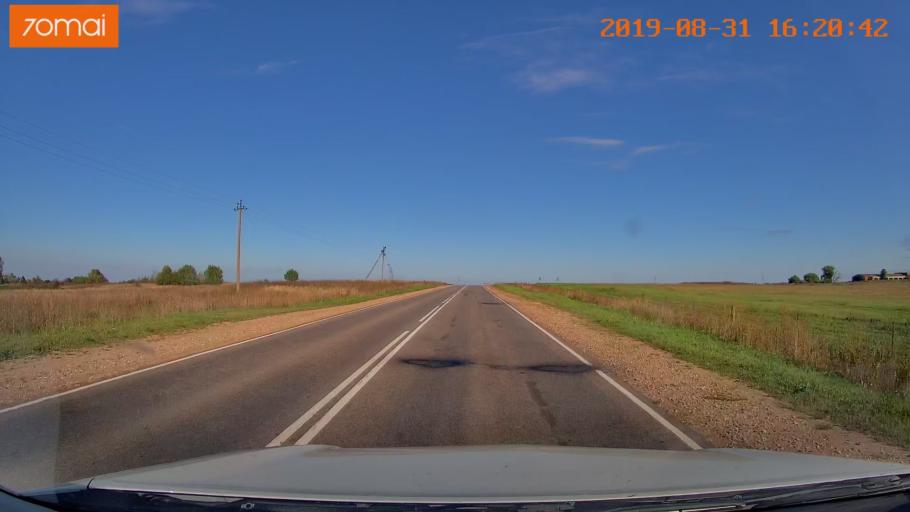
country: RU
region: Kaluga
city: Babynino
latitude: 54.5226
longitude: 35.6130
